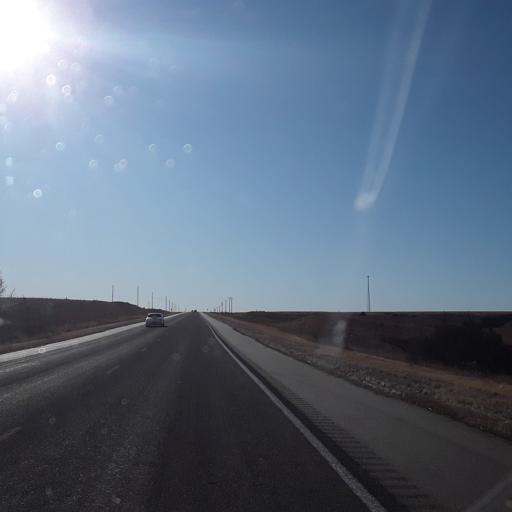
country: US
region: Nebraska
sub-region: Hitchcock County
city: Trenton
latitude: 40.2009
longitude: -100.9746
